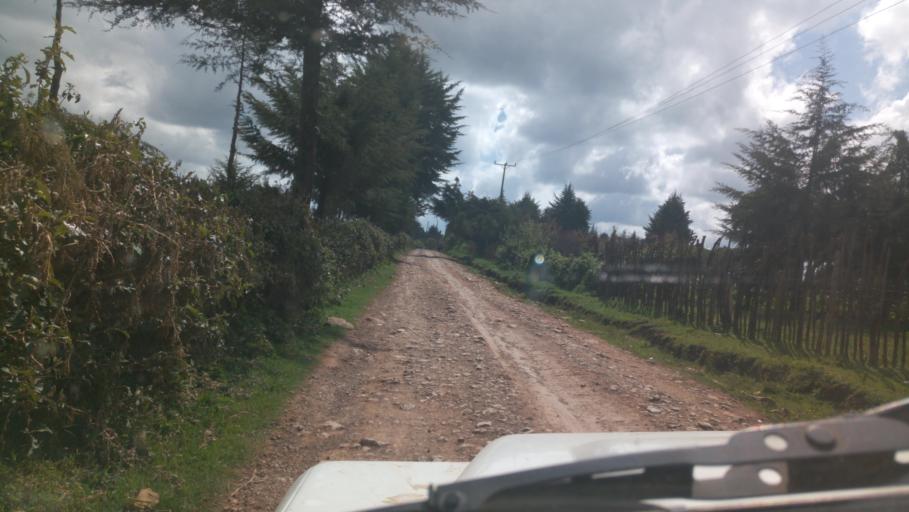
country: KE
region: Nakuru
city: Molo
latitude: -0.4745
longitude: 35.6812
